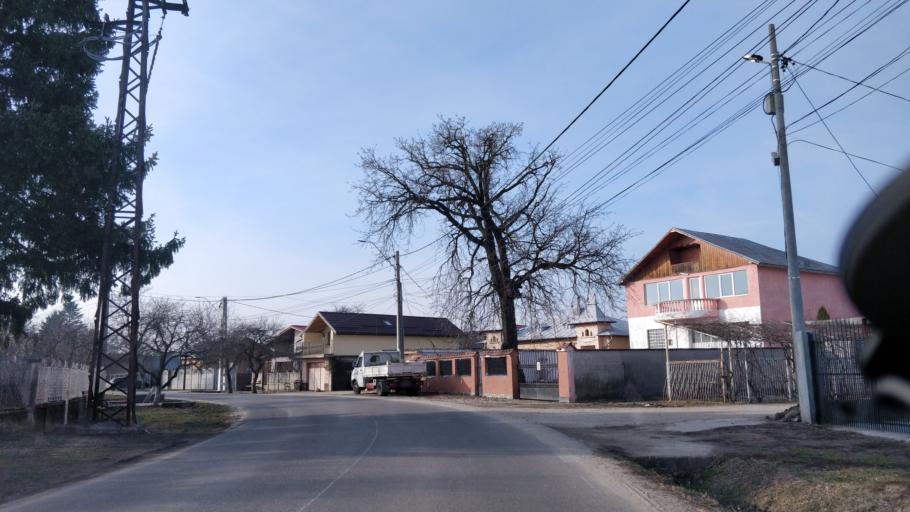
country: RO
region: Giurgiu
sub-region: Comuna Ulmi
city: Ulmi
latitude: 44.4829
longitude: 25.8039
